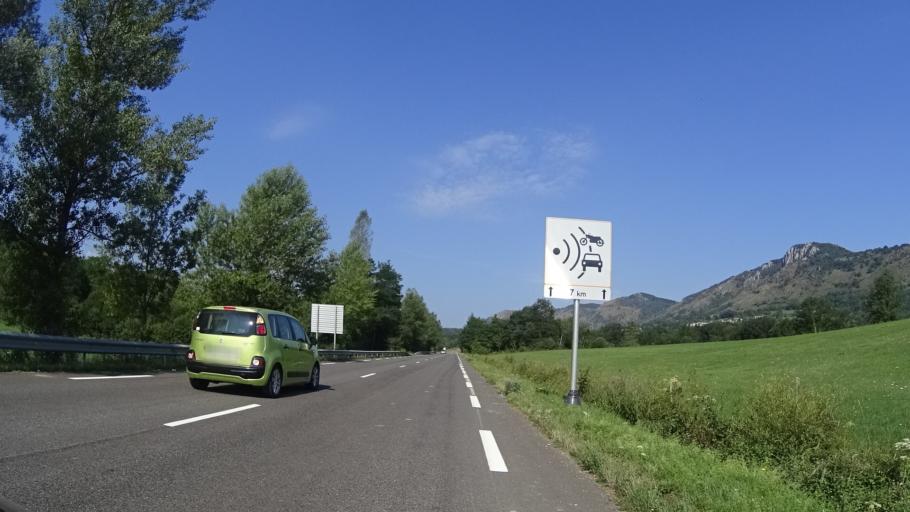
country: FR
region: Midi-Pyrenees
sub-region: Departement de l'Ariege
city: Saint-Paul-de-Jarrat
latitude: 42.9330
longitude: 1.7224
